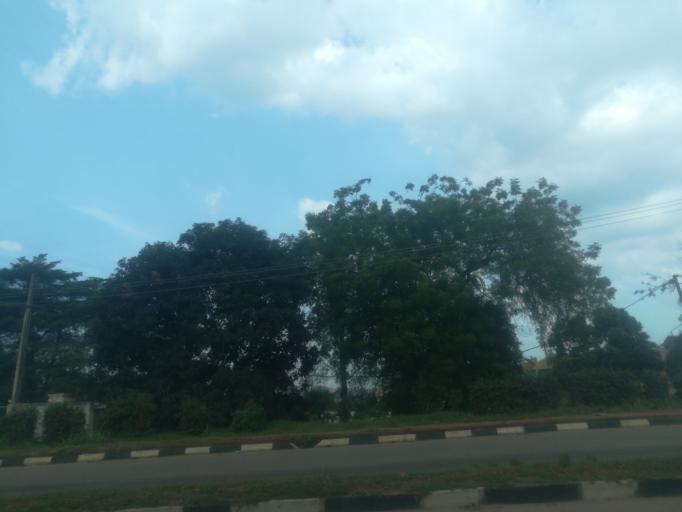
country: NG
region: Ogun
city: Abeokuta
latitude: 7.1379
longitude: 3.3425
